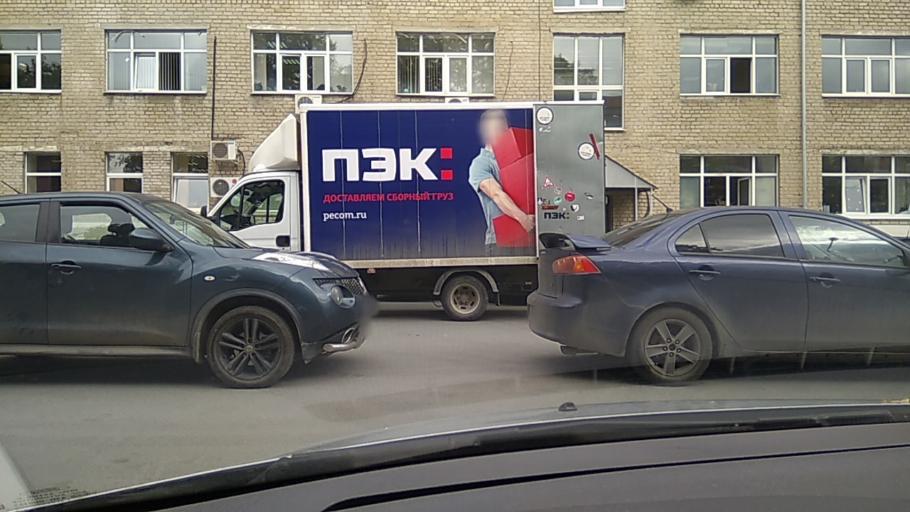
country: RU
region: Sverdlovsk
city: Yekaterinburg
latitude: 56.8246
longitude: 60.6446
